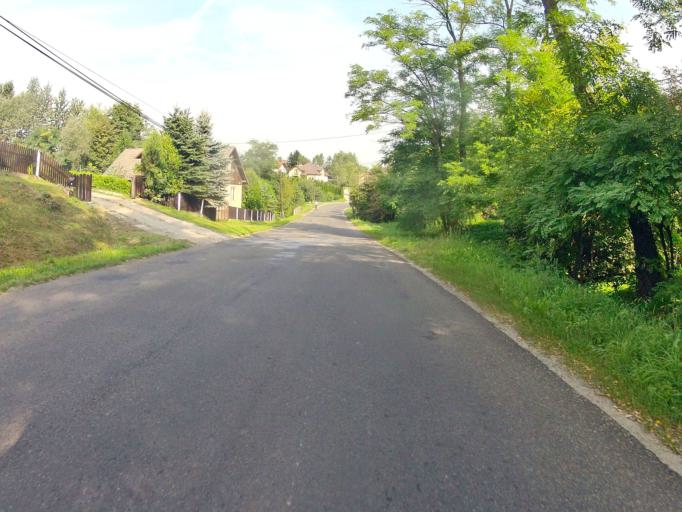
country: PL
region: Subcarpathian Voivodeship
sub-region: Powiat jasielski
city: Trzcinica
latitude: 49.7788
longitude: 21.4054
